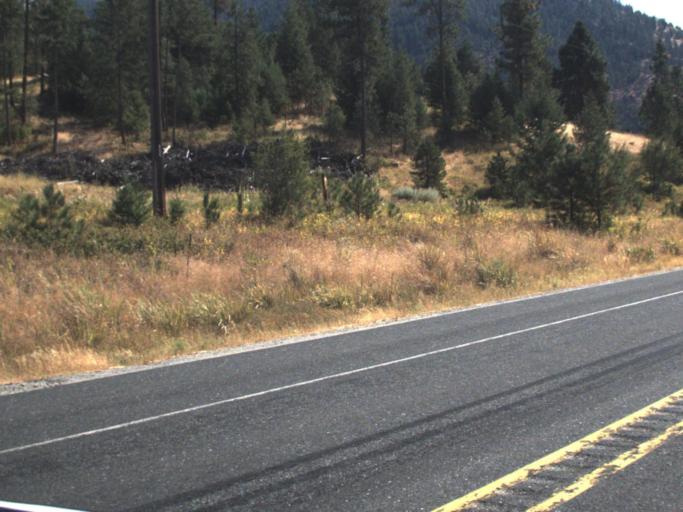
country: US
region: Washington
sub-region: Stevens County
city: Colville
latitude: 48.3992
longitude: -117.8495
